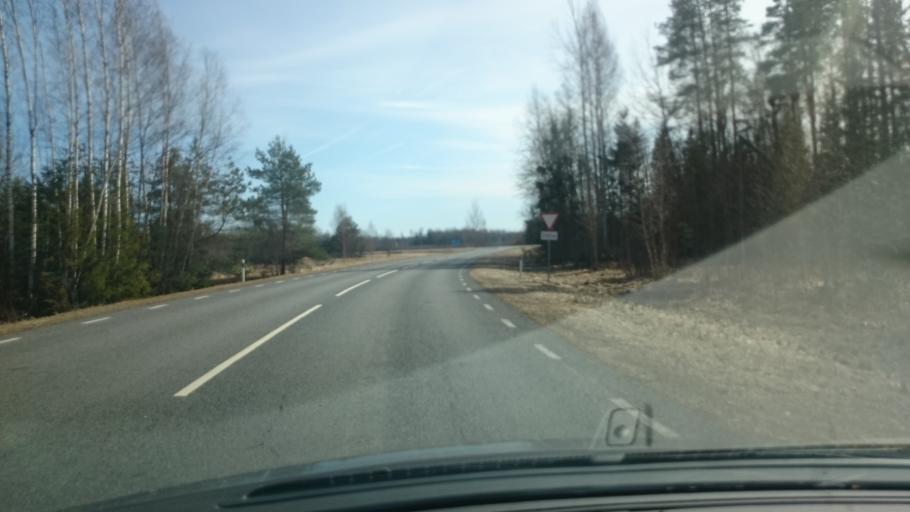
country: EE
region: Paernumaa
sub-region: Vaendra vald (alev)
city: Vandra
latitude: 58.6272
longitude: 24.9342
